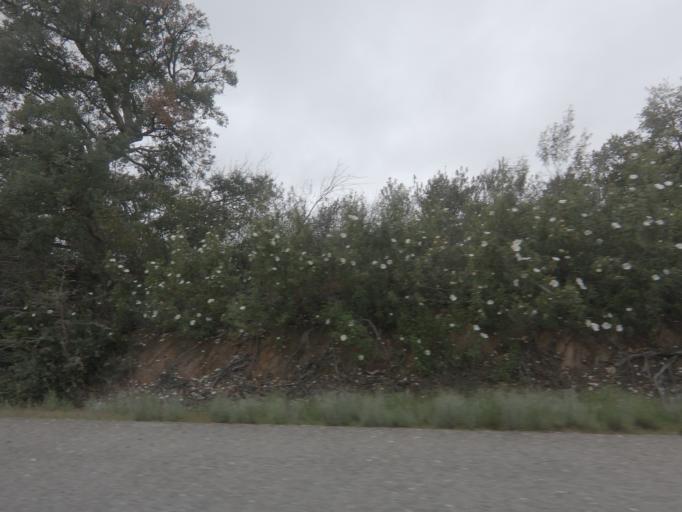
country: ES
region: Extremadura
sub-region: Provincia de Badajoz
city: Puebla de Obando
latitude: 39.2355
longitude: -6.5656
